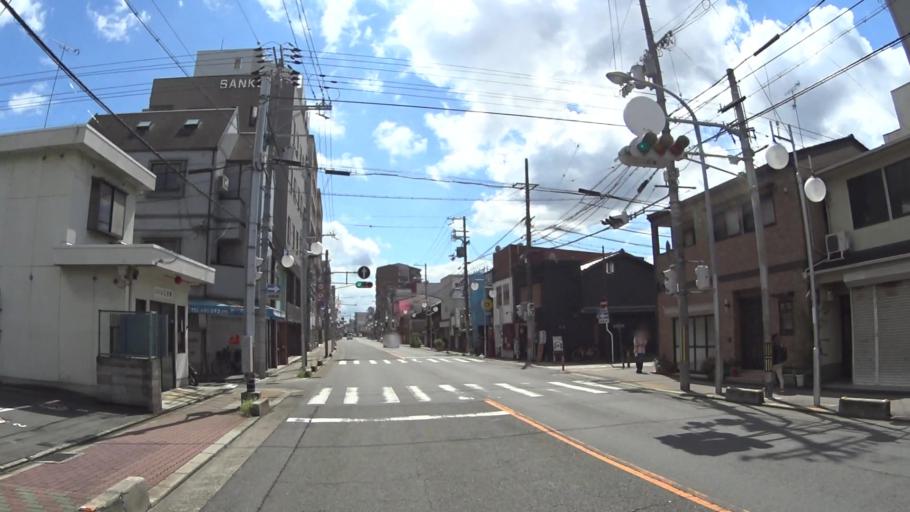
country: JP
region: Kyoto
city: Kyoto
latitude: 34.9822
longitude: 135.7611
